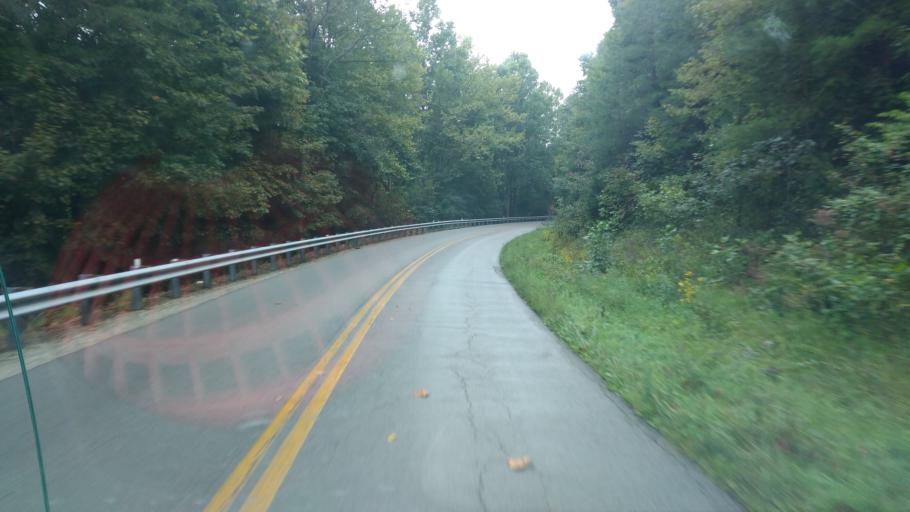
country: US
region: Kentucky
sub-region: Fleming County
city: Flemingsburg
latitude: 38.4356
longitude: -83.4966
